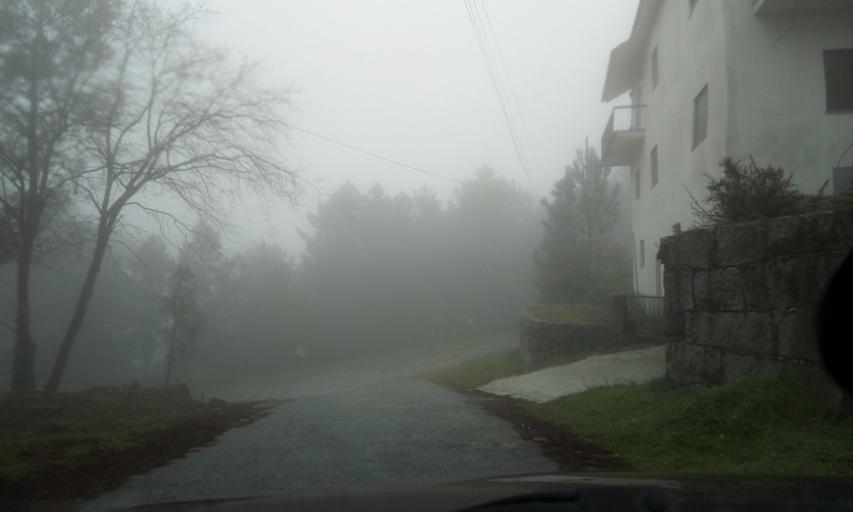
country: PT
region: Guarda
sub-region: Fornos de Algodres
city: Fornos de Algodres
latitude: 40.6285
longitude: -7.5393
